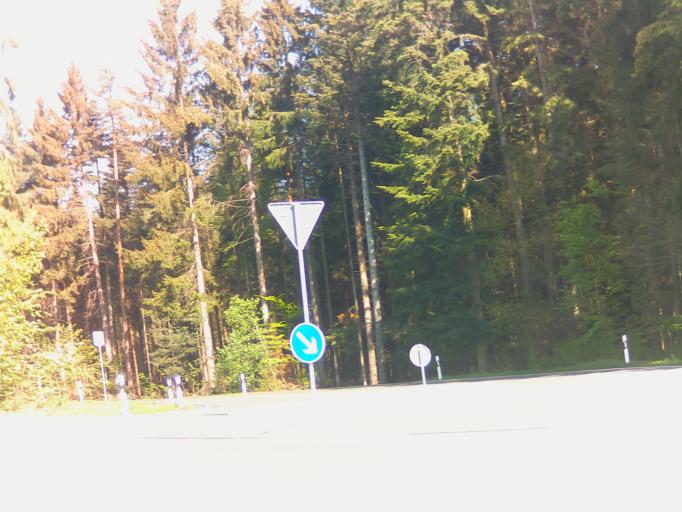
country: DE
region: Baden-Wuerttemberg
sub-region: Karlsruhe Region
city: Neuweiler
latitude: 48.6372
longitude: 8.6063
